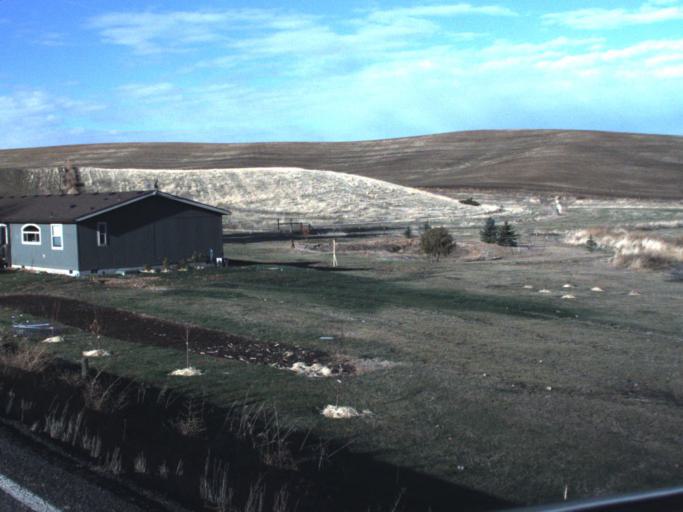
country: US
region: Washington
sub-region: Whitman County
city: Pullman
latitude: 46.7228
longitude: -117.2505
